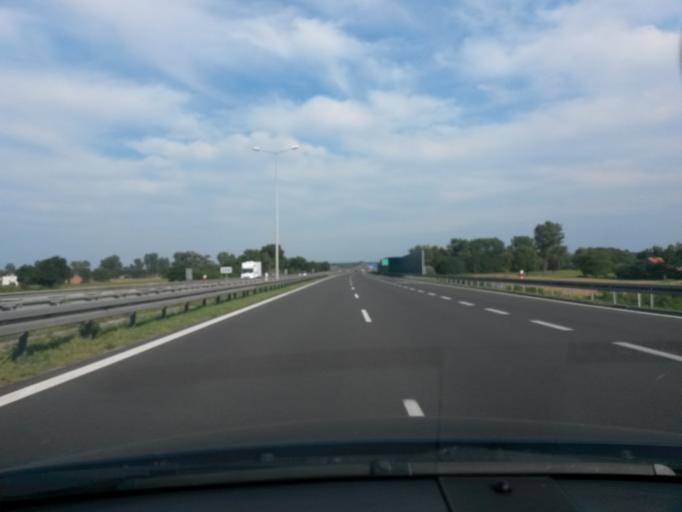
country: PL
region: Greater Poland Voivodeship
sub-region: Powiat koninski
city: Rzgow Pierwszy
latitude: 52.2039
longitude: 18.0254
